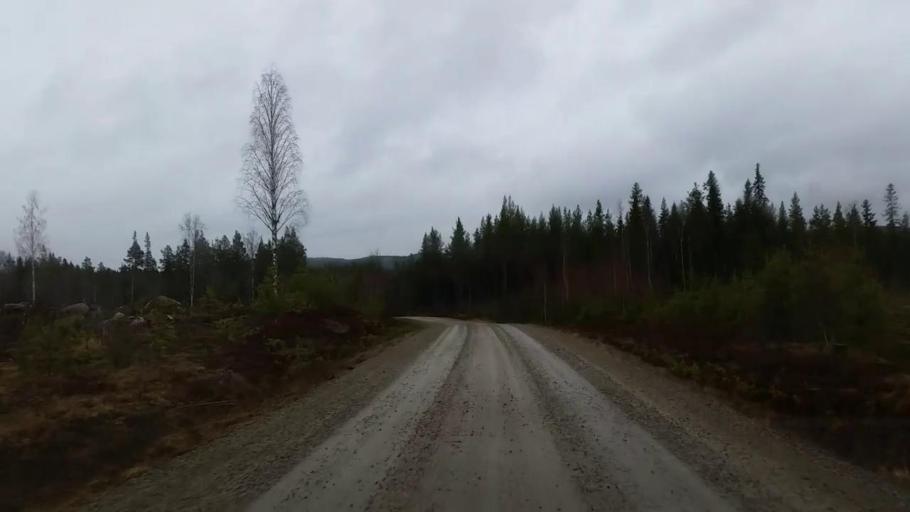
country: SE
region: Gaevleborg
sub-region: Ljusdals Kommun
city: Farila
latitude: 62.1280
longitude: 15.6660
